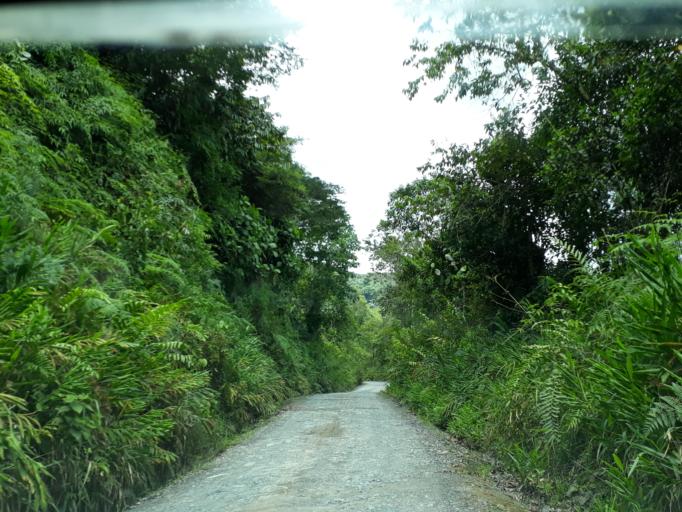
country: CO
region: Cundinamarca
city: Topaipi
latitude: 5.3483
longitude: -74.1927
